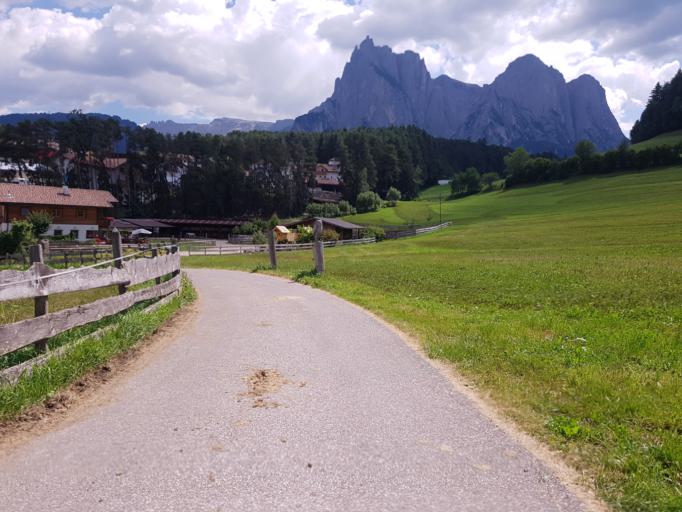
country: IT
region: Trentino-Alto Adige
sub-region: Bolzano
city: Castelrotto
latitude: 46.5575
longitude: 11.5507
